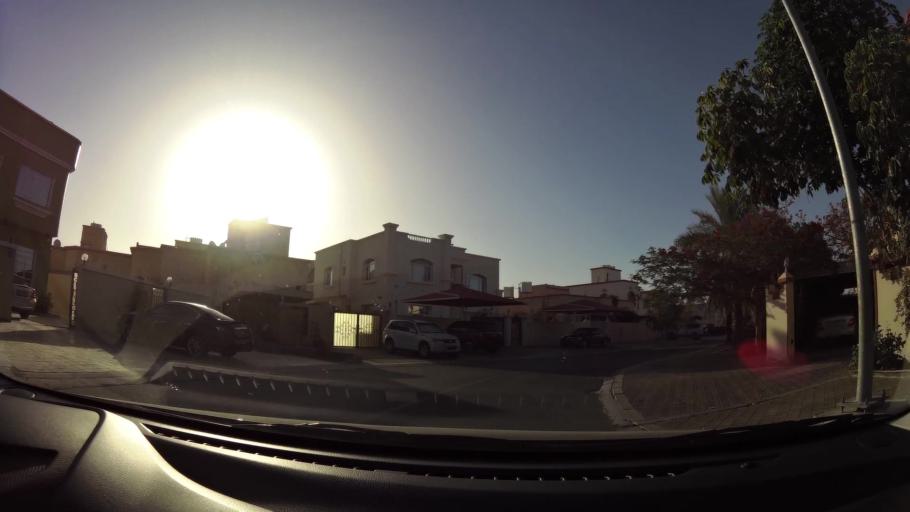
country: OM
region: Muhafazat Masqat
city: As Sib al Jadidah
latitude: 23.6104
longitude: 58.2174
